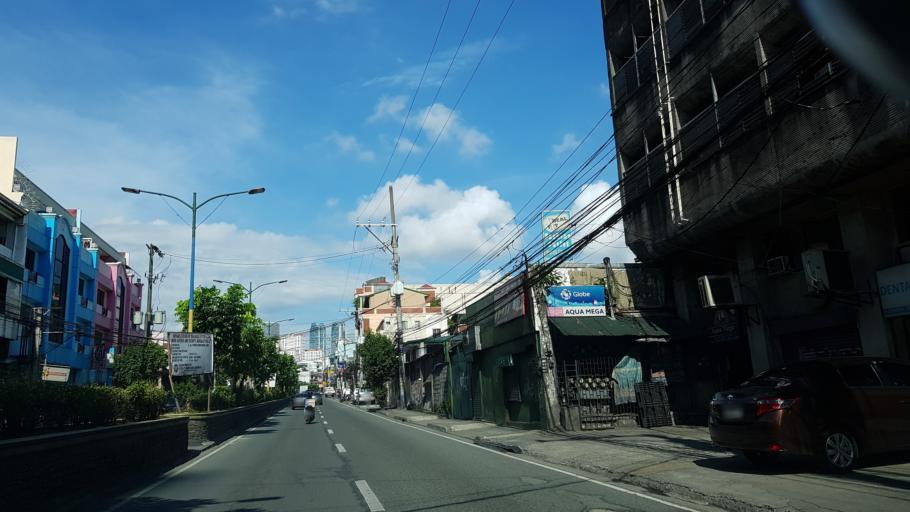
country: PH
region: Metro Manila
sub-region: Mandaluyong
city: Mandaluyong City
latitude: 14.5760
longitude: 121.0371
